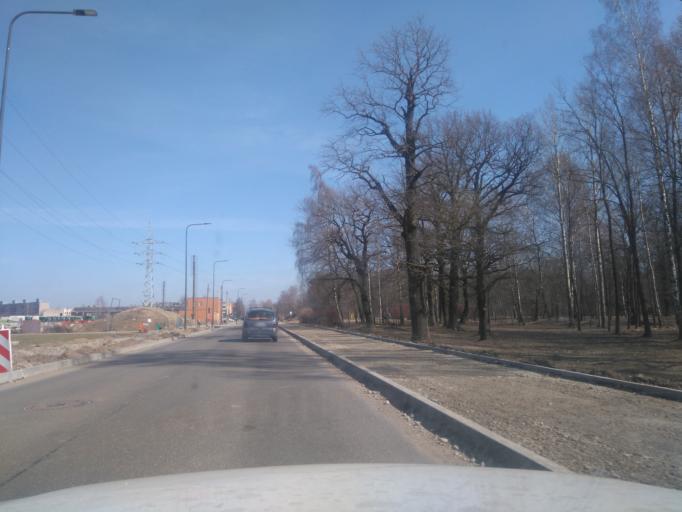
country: LT
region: Kauno apskritis
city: Dainava (Kaunas)
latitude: 54.8828
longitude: 23.9495
